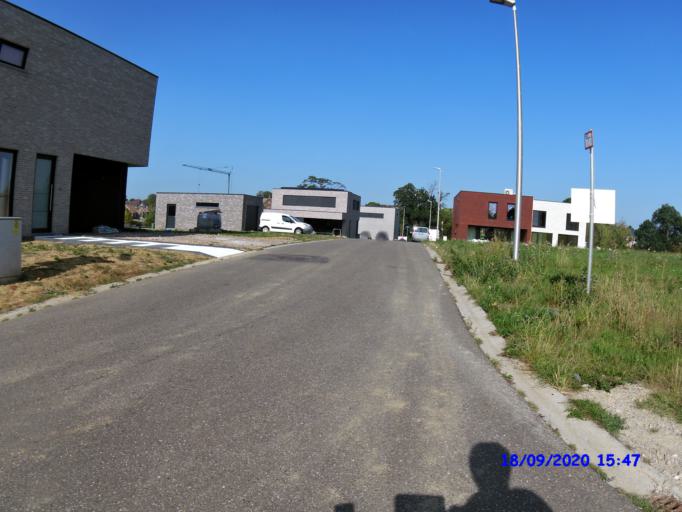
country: BE
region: Flanders
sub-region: Provincie Limburg
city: Gingelom
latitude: 50.7387
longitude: 5.1384
